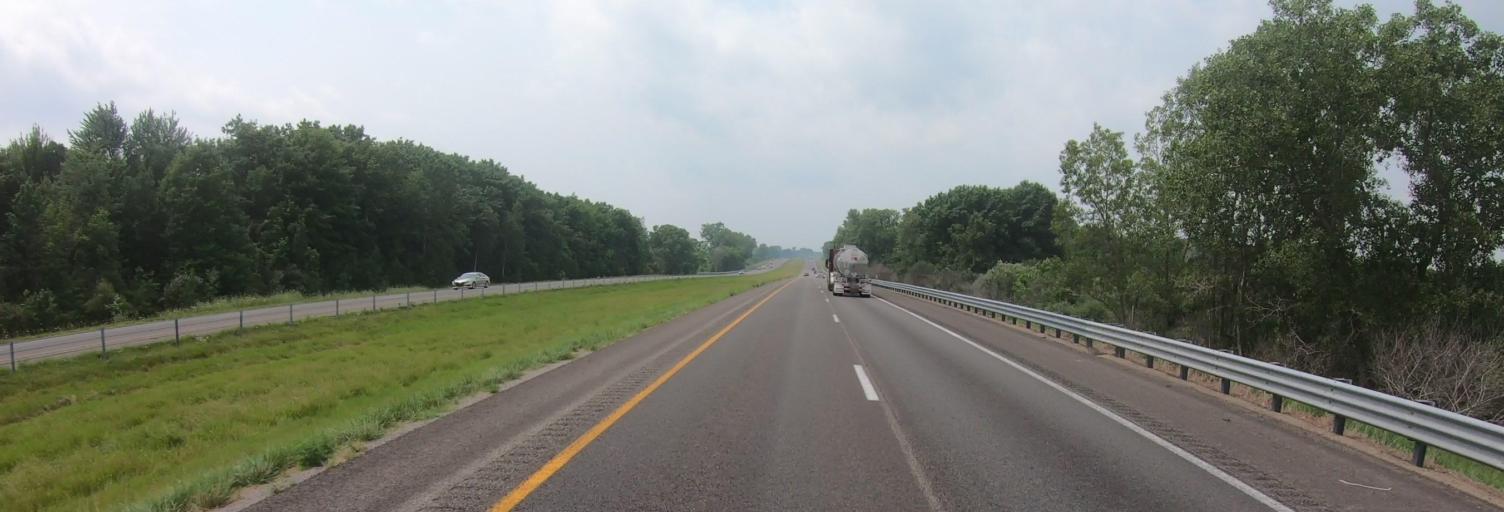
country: US
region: Michigan
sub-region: Shiawassee County
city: Durand
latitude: 42.9176
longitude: -84.0340
